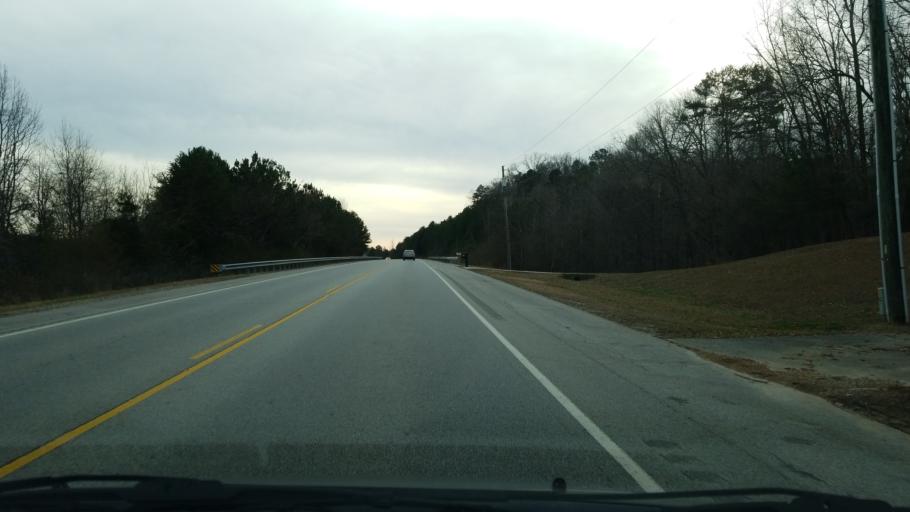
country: US
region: Tennessee
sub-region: Hamilton County
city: Collegedale
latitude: 35.0766
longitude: -85.0716
